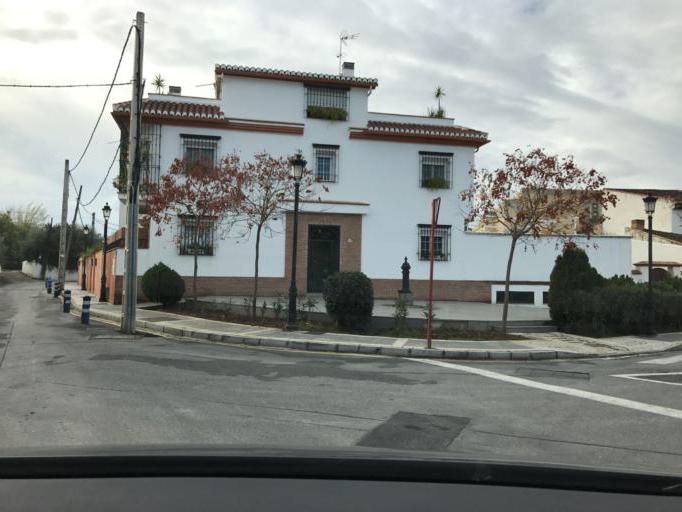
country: ES
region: Andalusia
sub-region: Provincia de Granada
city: Ogijares
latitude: 37.1237
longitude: -3.6032
